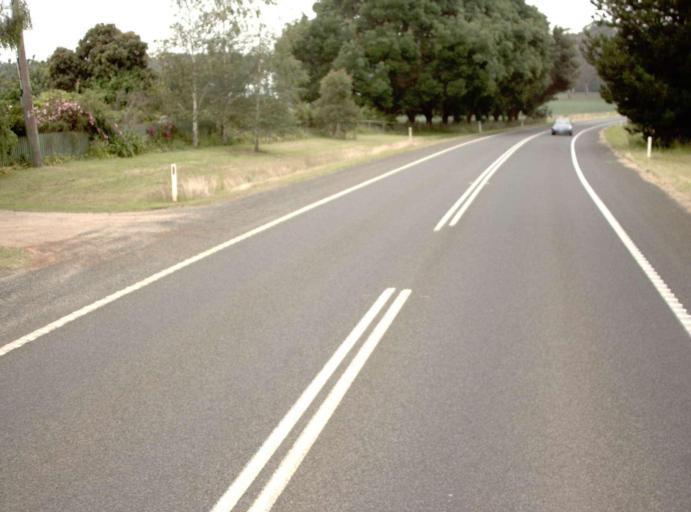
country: AU
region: Victoria
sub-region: Latrobe
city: Moe
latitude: -38.3334
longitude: 146.2259
